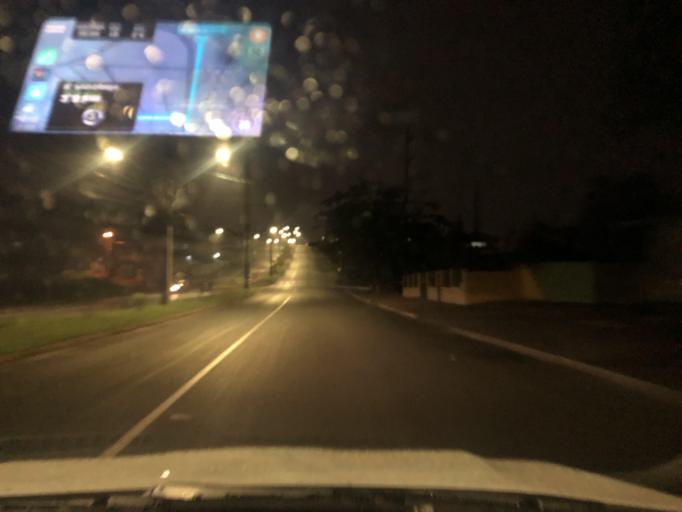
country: BR
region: Santa Catarina
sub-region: Joinville
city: Joinville
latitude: -26.3683
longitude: -48.8326
